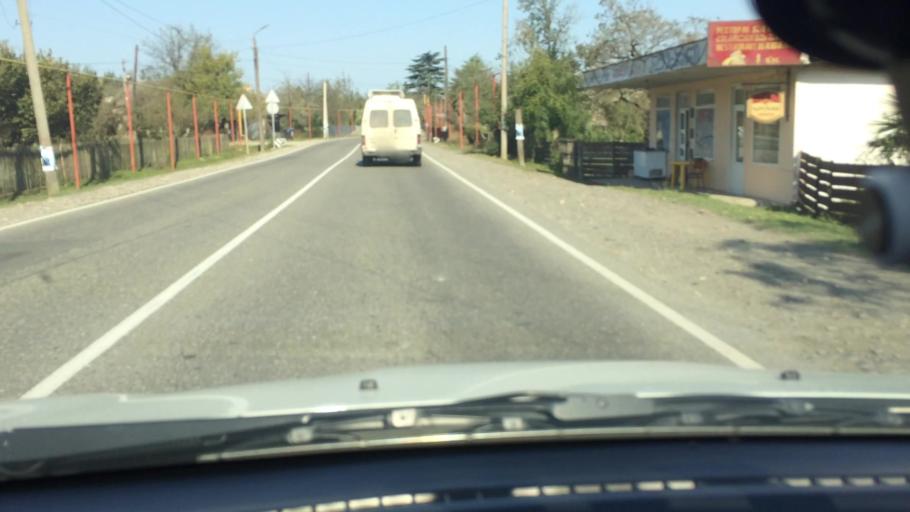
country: GE
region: Guria
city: Lanchkhuti
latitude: 42.0775
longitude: 42.0517
